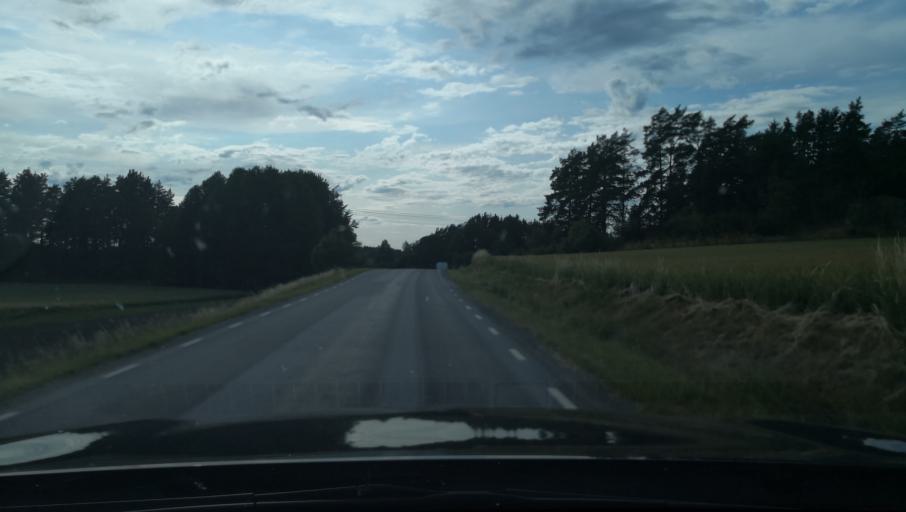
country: SE
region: Uppsala
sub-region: Enkopings Kommun
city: Orsundsbro
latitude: 59.6750
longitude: 17.4227
